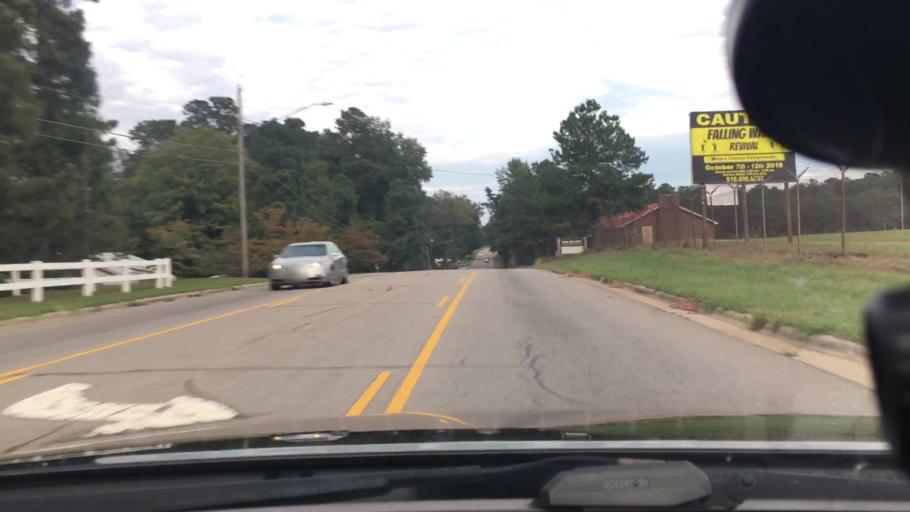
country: US
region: North Carolina
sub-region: Moore County
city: Carthage
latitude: 35.3449
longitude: -79.3896
